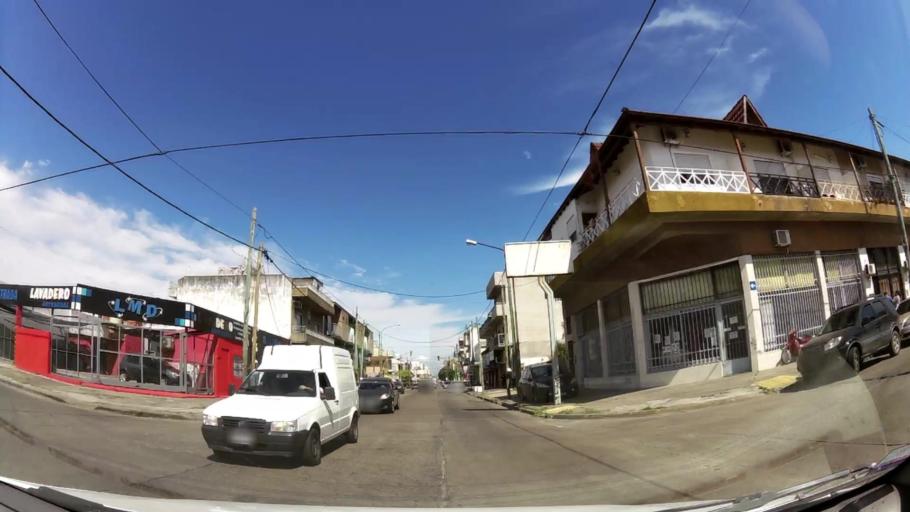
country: AR
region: Buenos Aires
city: San Justo
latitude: -34.6738
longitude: -58.5670
